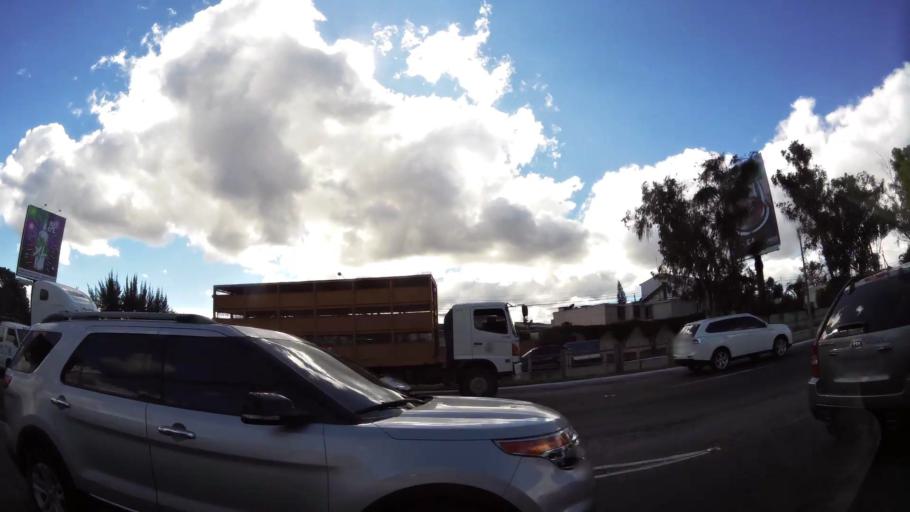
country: GT
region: Guatemala
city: Guatemala City
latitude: 14.6178
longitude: -90.5554
